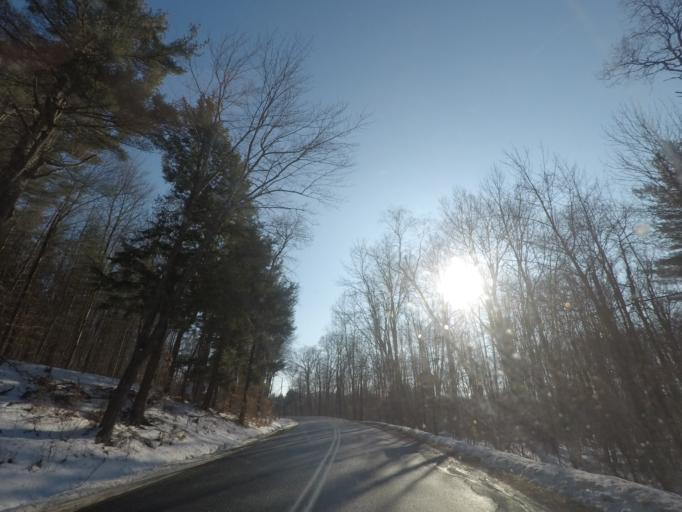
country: US
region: Massachusetts
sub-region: Berkshire County
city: Richmond
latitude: 42.5031
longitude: -73.4354
